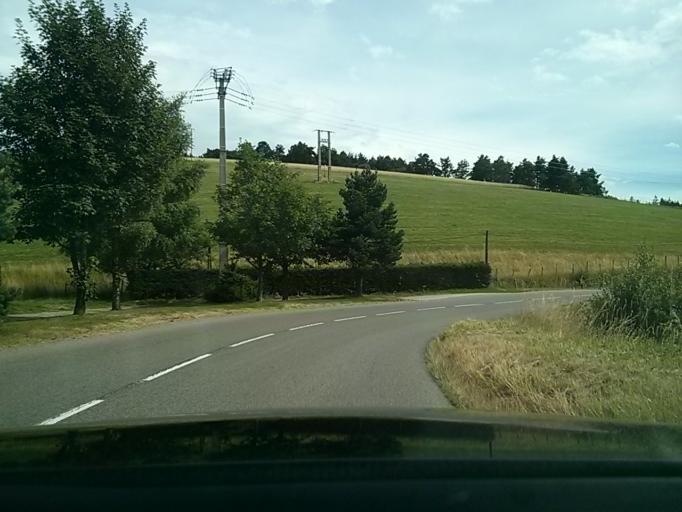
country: FR
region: Rhone-Alpes
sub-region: Departement de la Loire
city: Saint-Genest-Malifaux
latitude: 45.3759
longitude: 4.4909
